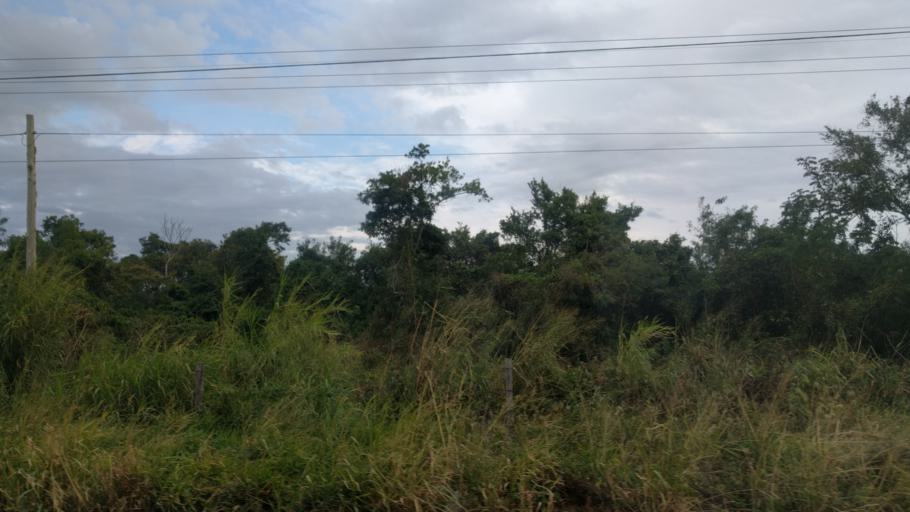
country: BO
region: Santa Cruz
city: Montero
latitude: -17.3870
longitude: -63.2203
